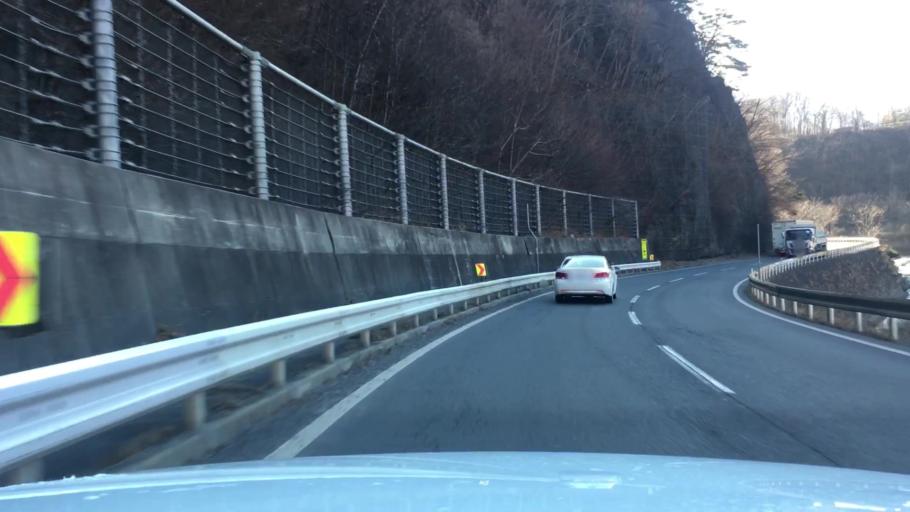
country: JP
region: Iwate
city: Miyako
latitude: 39.6110
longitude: 141.6494
